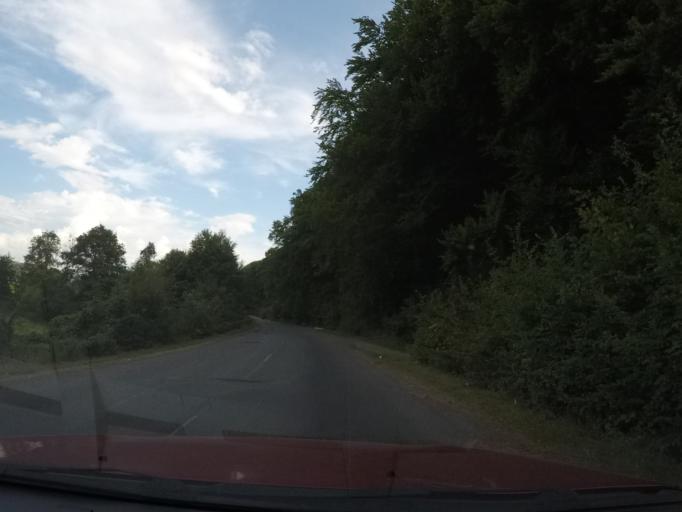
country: UA
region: Zakarpattia
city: Velykyi Bereznyi
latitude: 48.9211
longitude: 22.4553
